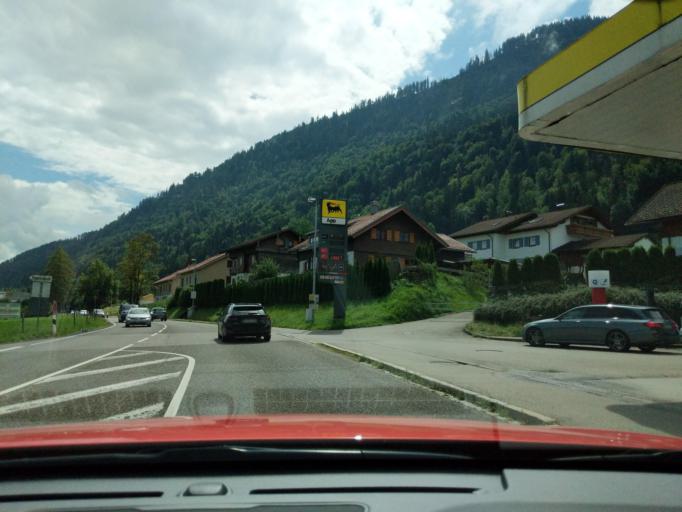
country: DE
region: Bavaria
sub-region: Swabia
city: Immenstadt im Allgau
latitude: 47.5672
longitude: 10.1929
